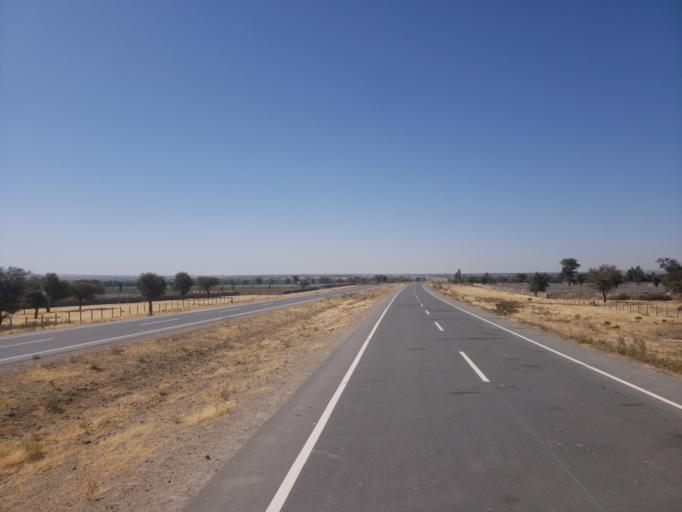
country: ET
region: Oromiya
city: Mojo
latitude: 8.3501
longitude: 38.9821
